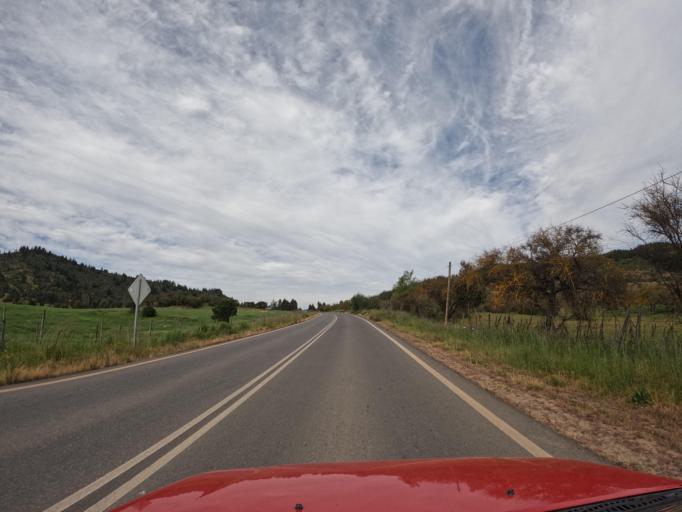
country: CL
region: Maule
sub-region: Provincia de Talca
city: Talca
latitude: -35.3229
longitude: -71.9503
